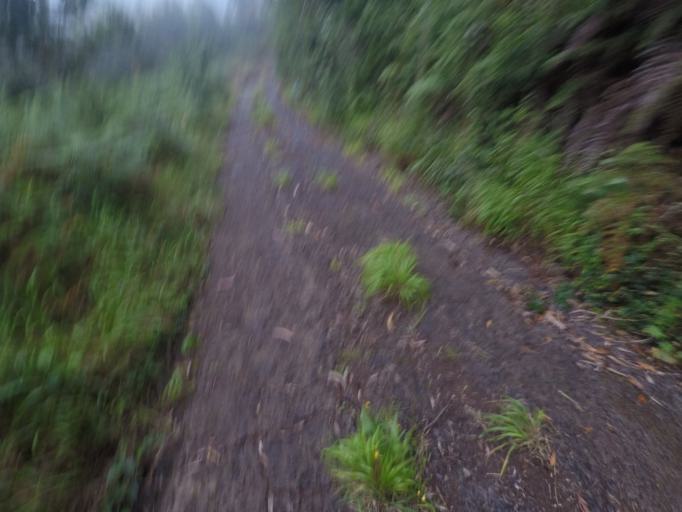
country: PT
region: Madeira
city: Ponta do Sol
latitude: 32.7096
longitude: -17.0933
